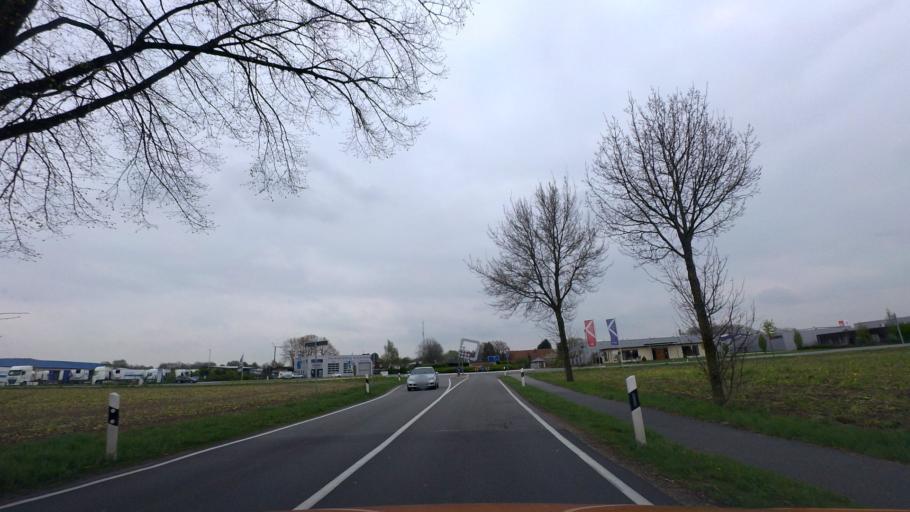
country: DE
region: Lower Saxony
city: Neuenkirchen
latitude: 52.4987
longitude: 8.0693
